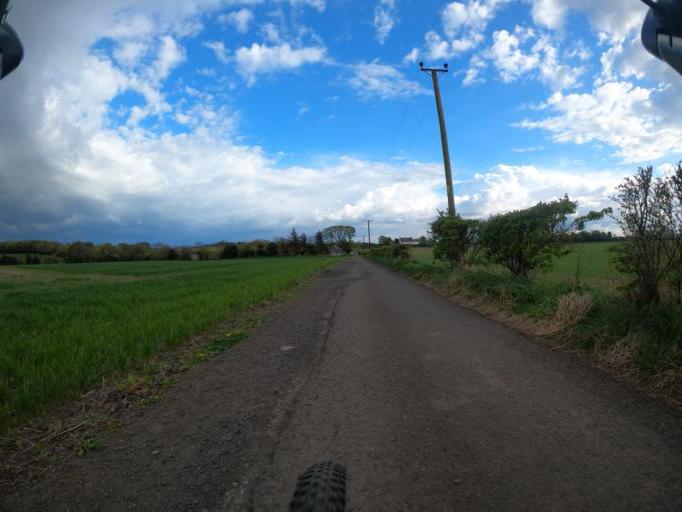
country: GB
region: Scotland
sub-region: Edinburgh
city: Ratho
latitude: 55.9598
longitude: -3.3398
